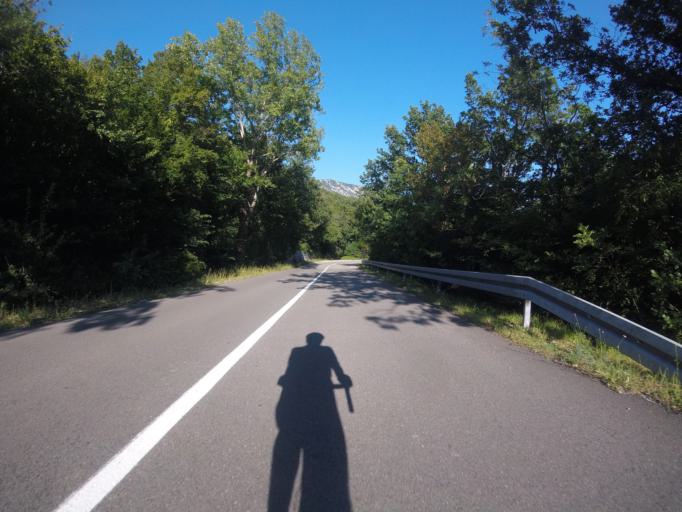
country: HR
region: Primorsko-Goranska
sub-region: Grad Crikvenica
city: Jadranovo
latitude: 45.2463
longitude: 14.6357
